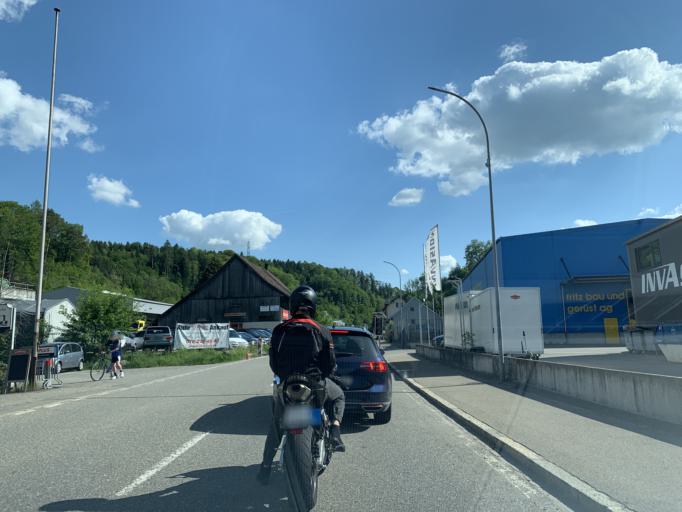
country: CH
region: Zurich
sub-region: Bezirk Pfaeffikon
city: Effretikon / Watt
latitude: 47.4435
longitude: 8.7043
